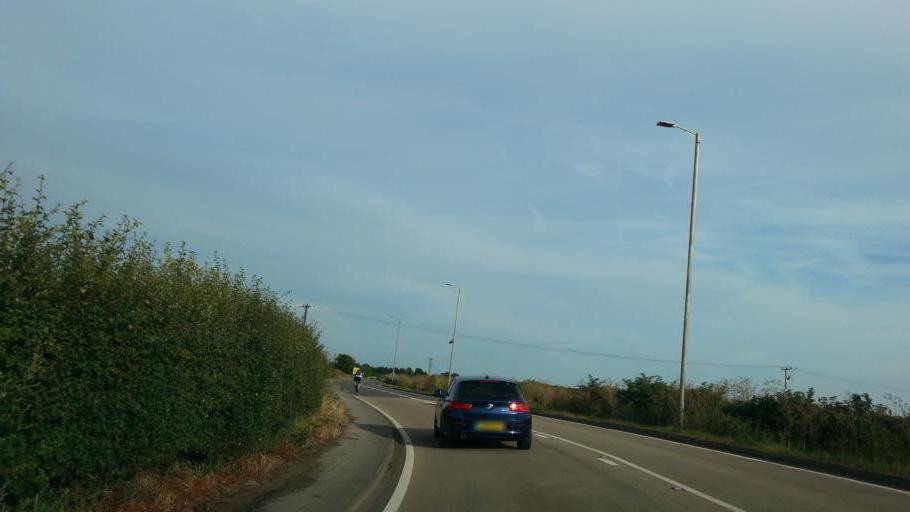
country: GB
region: England
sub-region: Nottinghamshire
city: Newark on Trent
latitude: 53.0892
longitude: -0.8416
